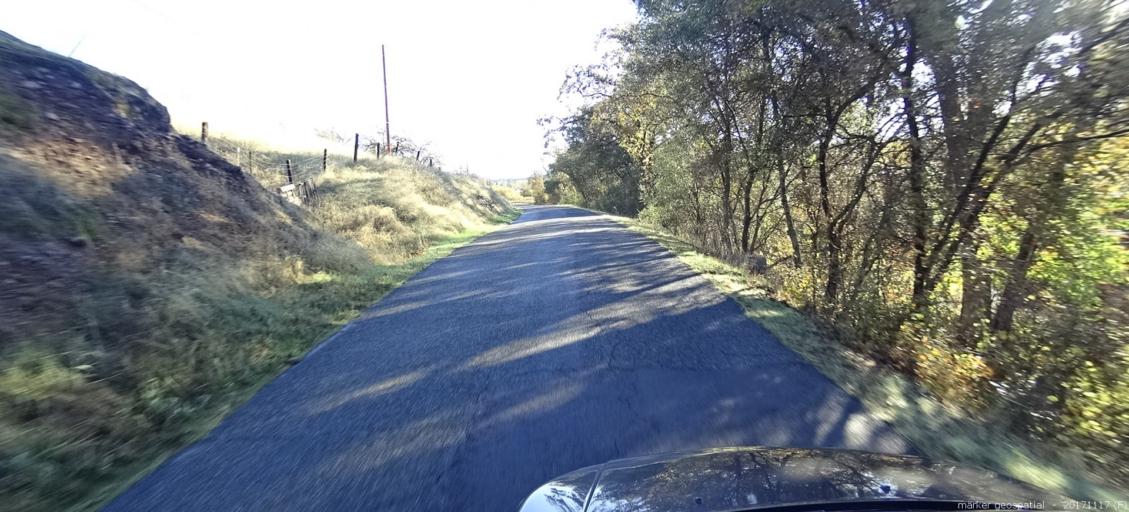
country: US
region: California
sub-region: Shasta County
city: Cottonwood
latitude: 40.3989
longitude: -122.1578
